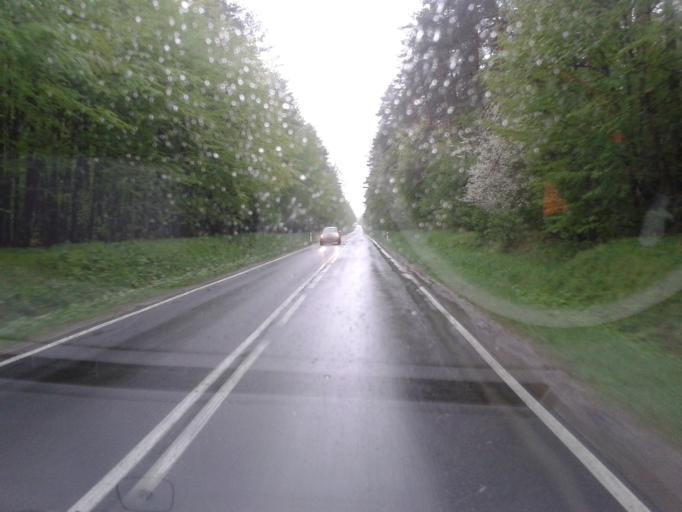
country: PL
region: Subcarpathian Voivodeship
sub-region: Powiat lubaczowski
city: Narol
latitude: 50.3189
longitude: 23.2646
